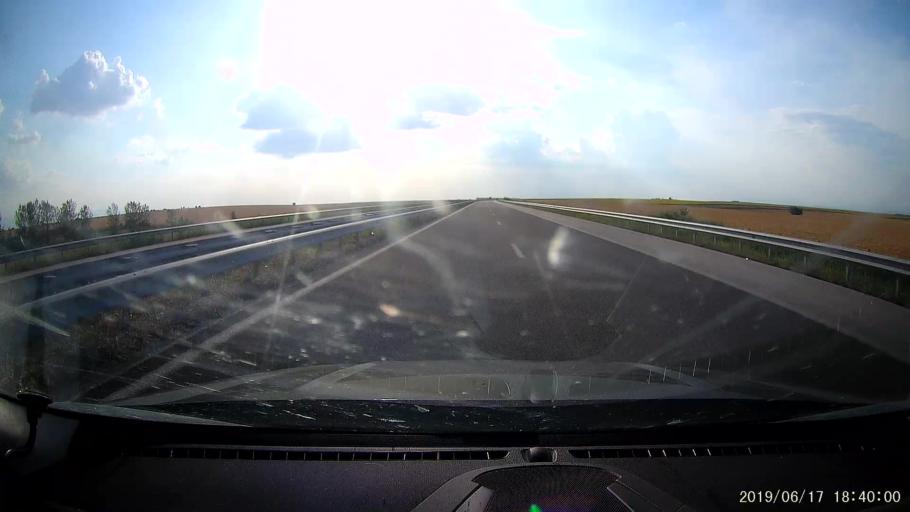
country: BG
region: Stara Zagora
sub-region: Obshtina Chirpan
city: Chirpan
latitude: 42.1505
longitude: 25.2906
